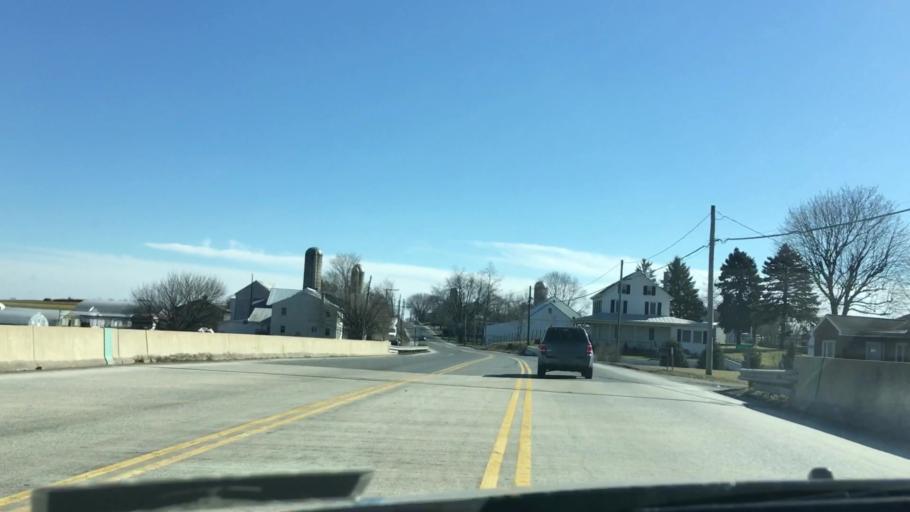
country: US
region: Pennsylvania
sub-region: Lancaster County
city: Ephrata
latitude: 40.1529
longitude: -76.1275
